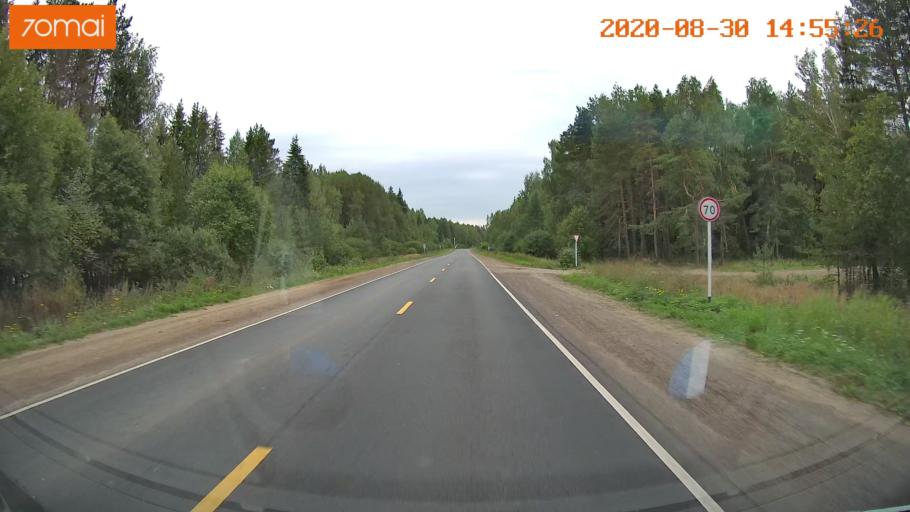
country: RU
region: Ivanovo
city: Kineshma
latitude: 57.3844
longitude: 42.0361
